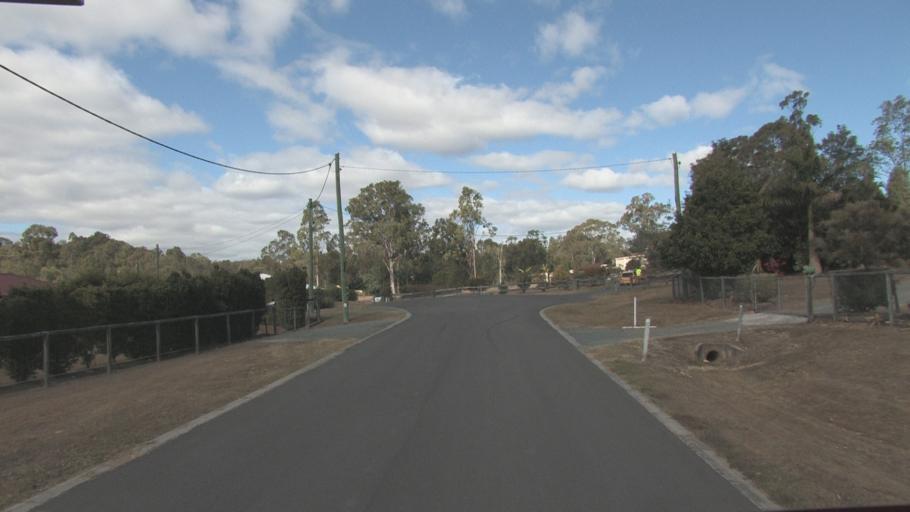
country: AU
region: Queensland
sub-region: Logan
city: Cedar Vale
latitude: -27.8740
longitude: 152.9994
